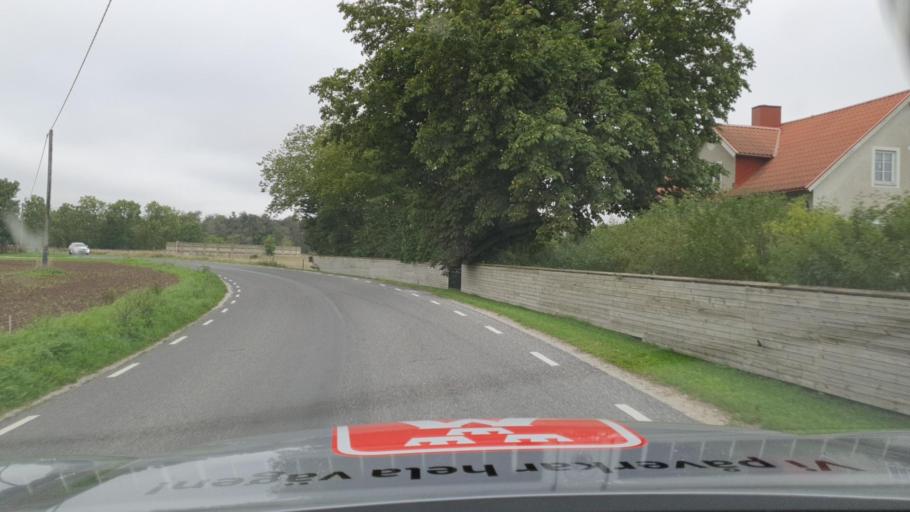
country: SE
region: Gotland
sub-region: Gotland
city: Visby
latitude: 57.6658
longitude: 18.4668
